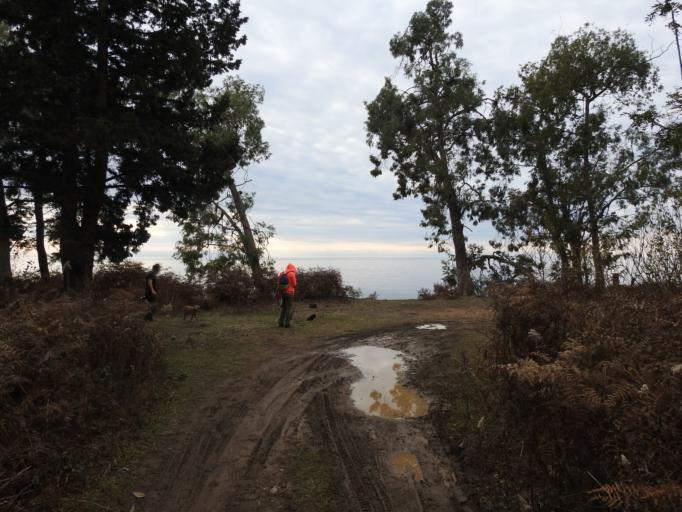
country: GE
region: Abkhazia
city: Dranda
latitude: 42.7935
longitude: 41.2562
